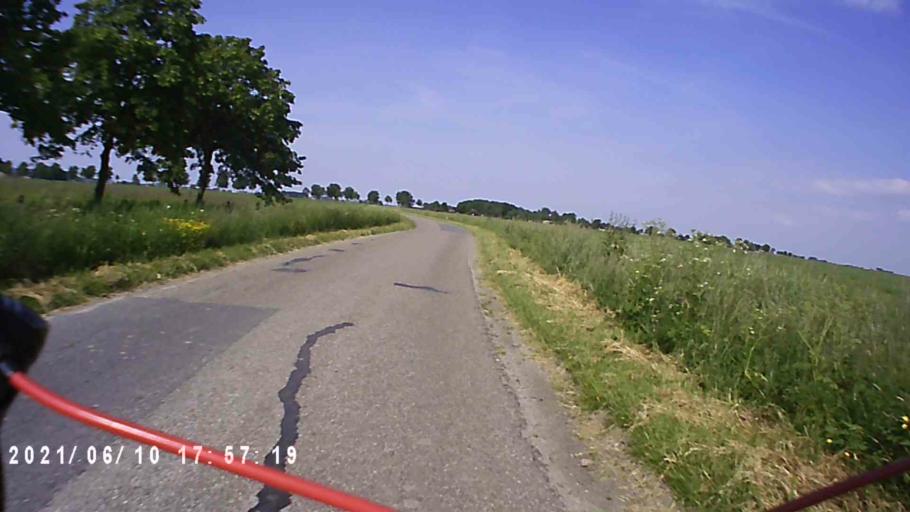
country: NL
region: Groningen
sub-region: Gemeente De Marne
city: Ulrum
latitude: 53.3327
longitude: 6.3294
